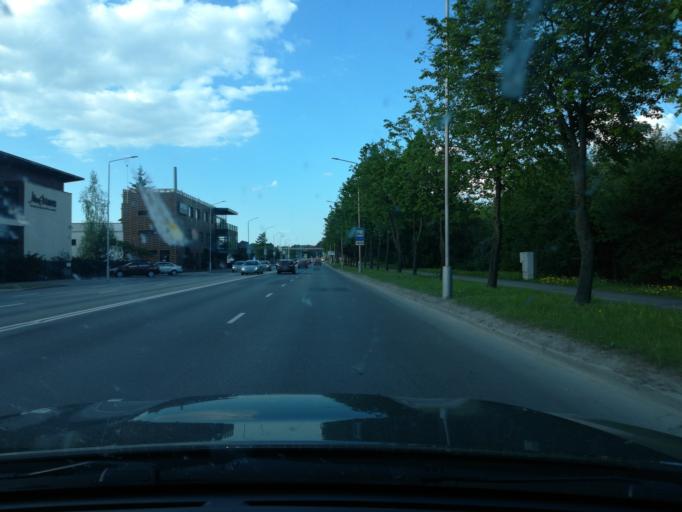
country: LT
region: Kauno apskritis
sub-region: Kaunas
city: Eiguliai
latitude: 54.9318
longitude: 23.9173
